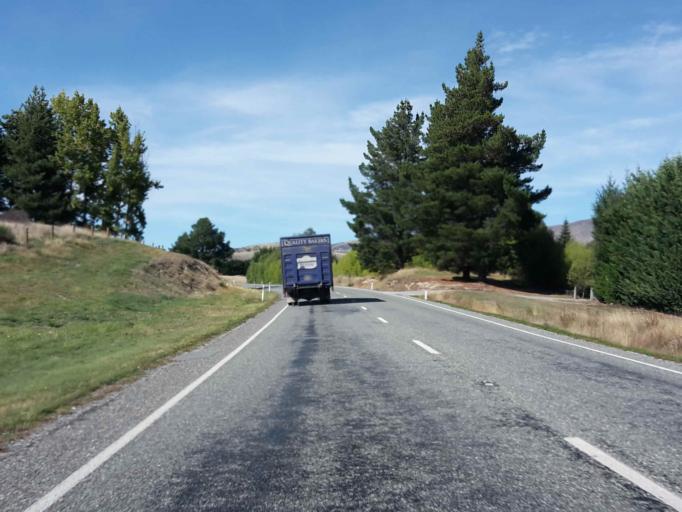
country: NZ
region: Otago
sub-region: Queenstown-Lakes District
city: Wanaka
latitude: -44.7126
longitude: 169.2094
